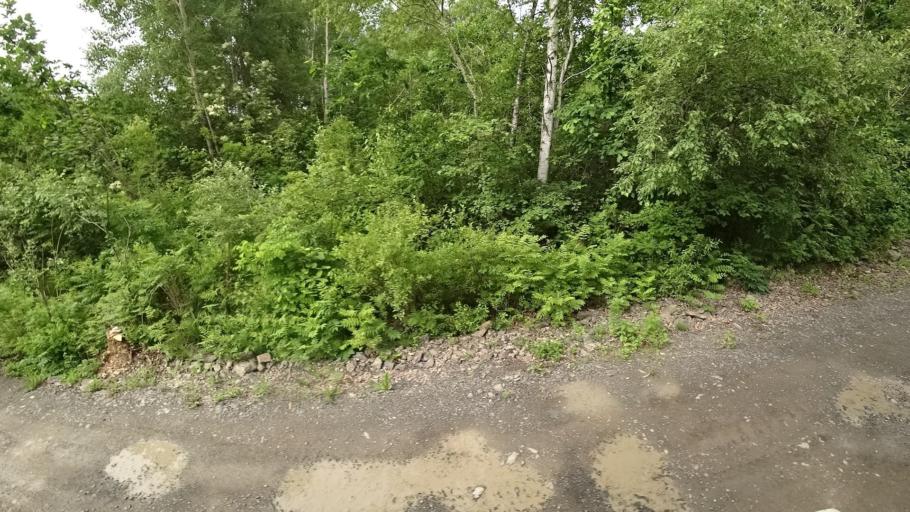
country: RU
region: Khabarovsk Krai
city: Amursk
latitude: 49.9000
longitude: 136.1502
